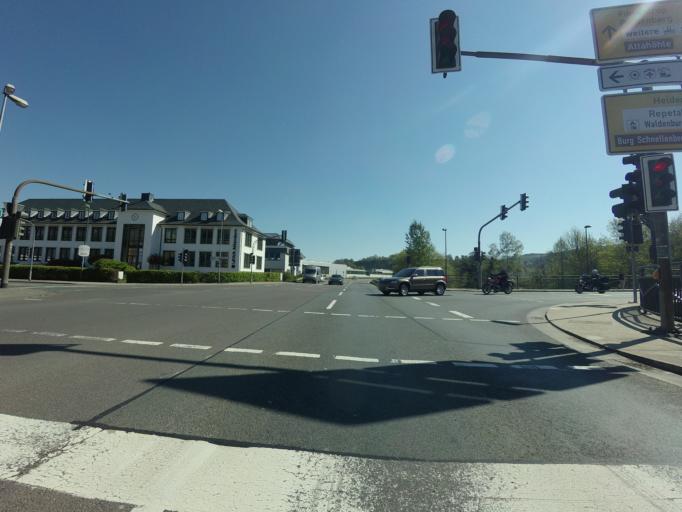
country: DE
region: North Rhine-Westphalia
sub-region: Regierungsbezirk Arnsberg
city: Attendorn
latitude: 51.1231
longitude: 7.9060
